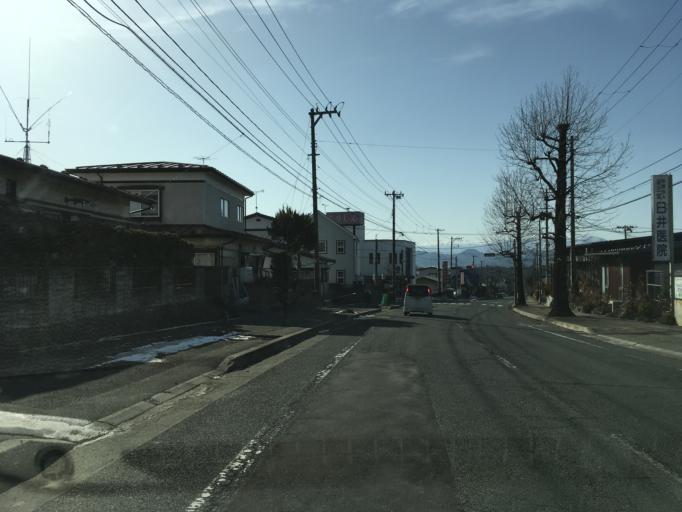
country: JP
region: Iwate
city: Morioka-shi
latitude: 39.7475
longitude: 141.1658
